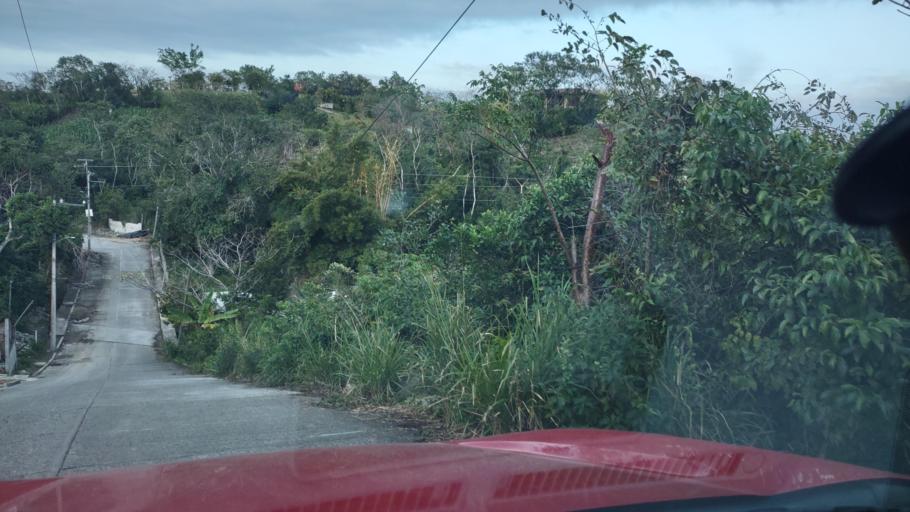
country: MX
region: Veracruz
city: Papantla de Olarte
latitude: 20.4535
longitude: -97.3062
